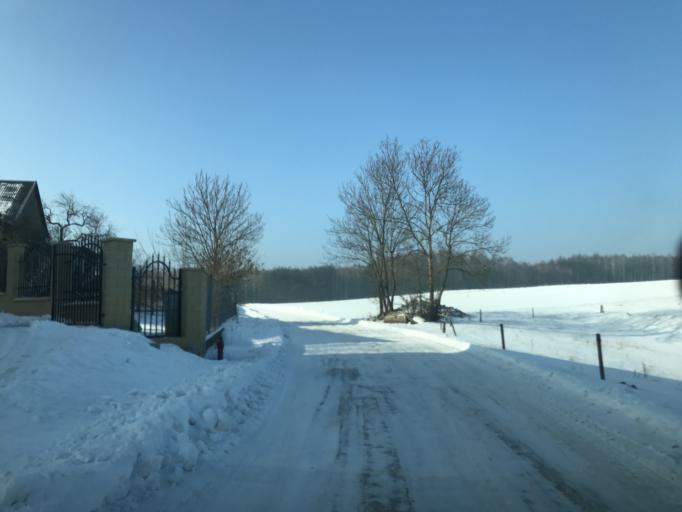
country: PL
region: Warmian-Masurian Voivodeship
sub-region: Powiat dzialdowski
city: Lidzbark
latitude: 53.2405
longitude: 19.8005
